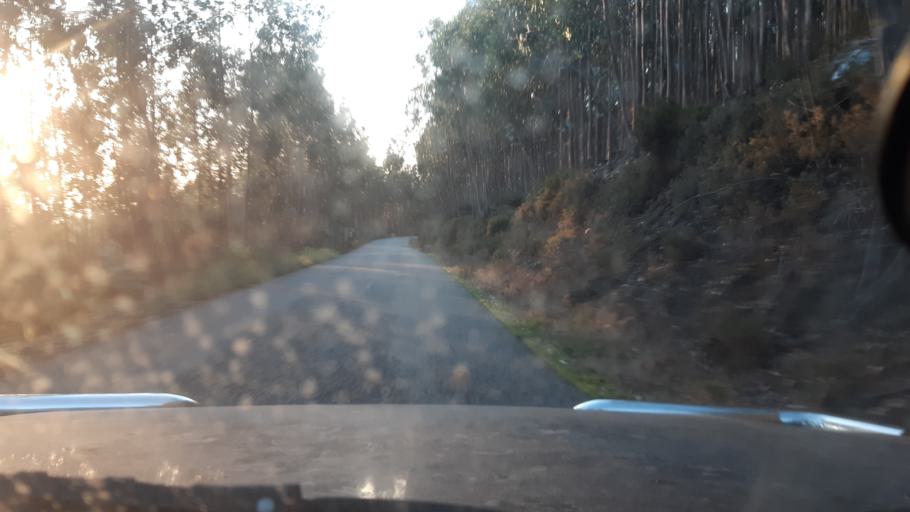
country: PT
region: Aveiro
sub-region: Agueda
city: Aguada de Cima
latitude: 40.5571
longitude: -8.2918
